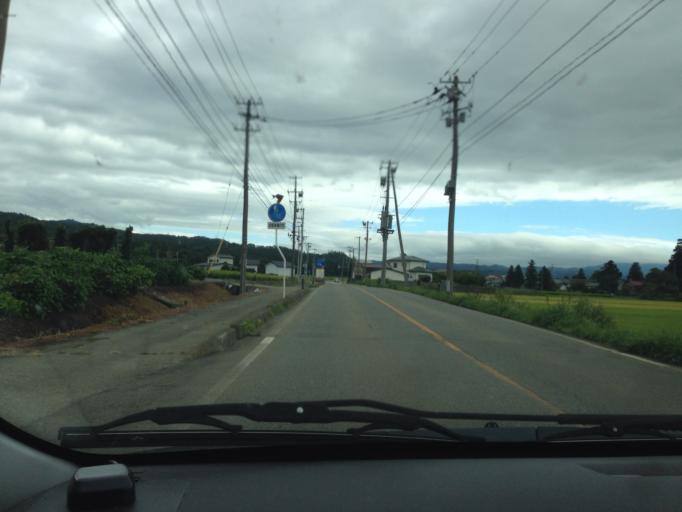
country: JP
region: Fukushima
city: Kitakata
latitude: 37.5907
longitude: 139.9063
